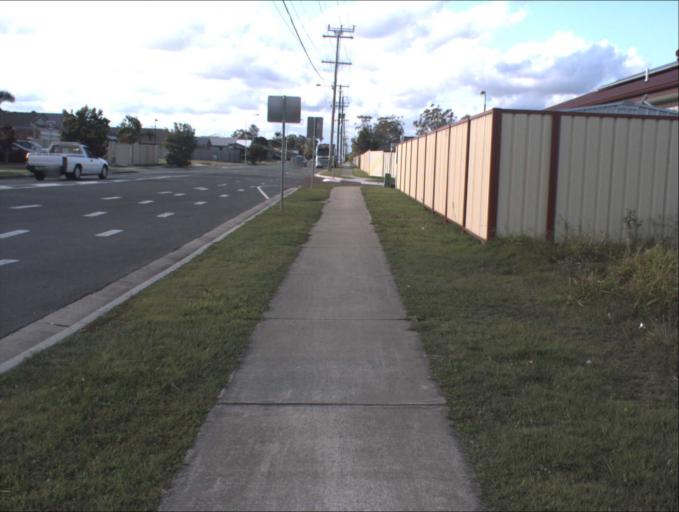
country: AU
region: Queensland
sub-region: Logan
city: Logan Reserve
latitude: -27.6787
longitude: 153.0849
